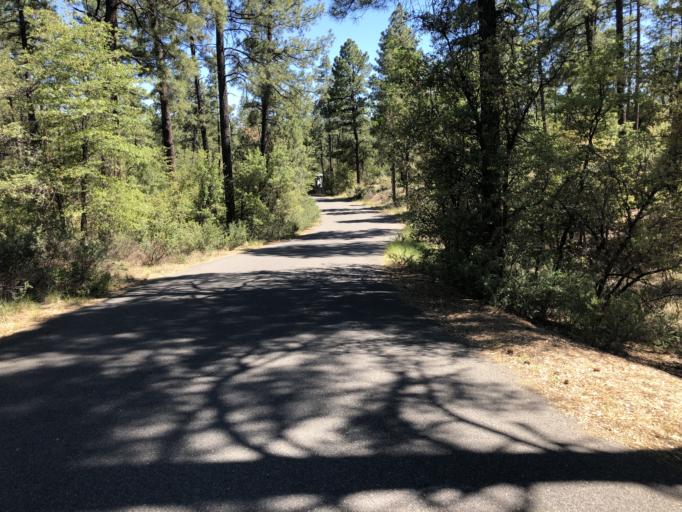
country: US
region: Arizona
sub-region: Yavapai County
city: Prescott
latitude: 34.5165
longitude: -112.3888
